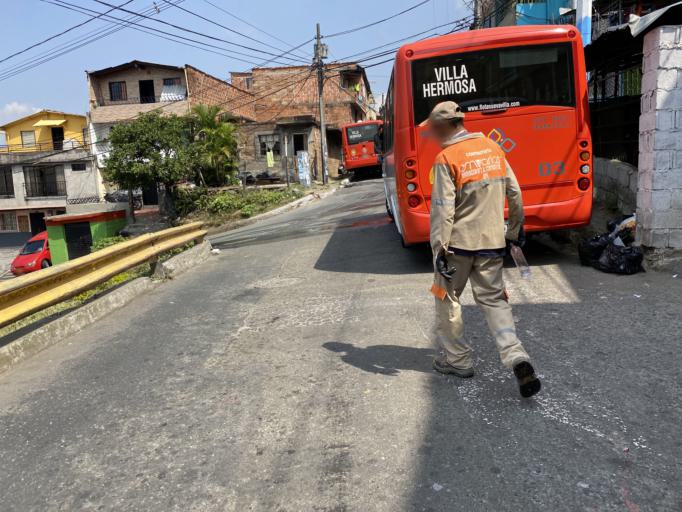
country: CO
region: Antioquia
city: Medellin
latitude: 6.2659
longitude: -75.5430
